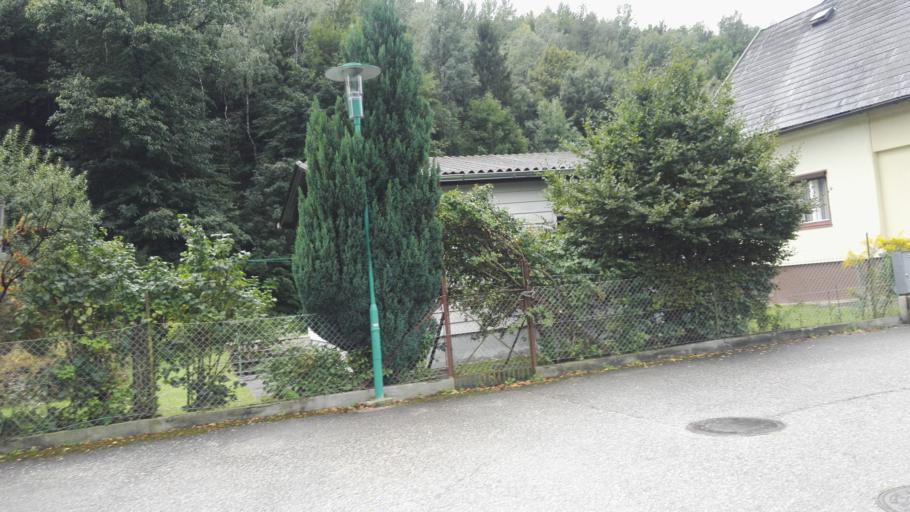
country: AT
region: Lower Austria
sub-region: Politischer Bezirk Neunkirchen
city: Payerbach
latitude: 47.6898
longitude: 15.8701
